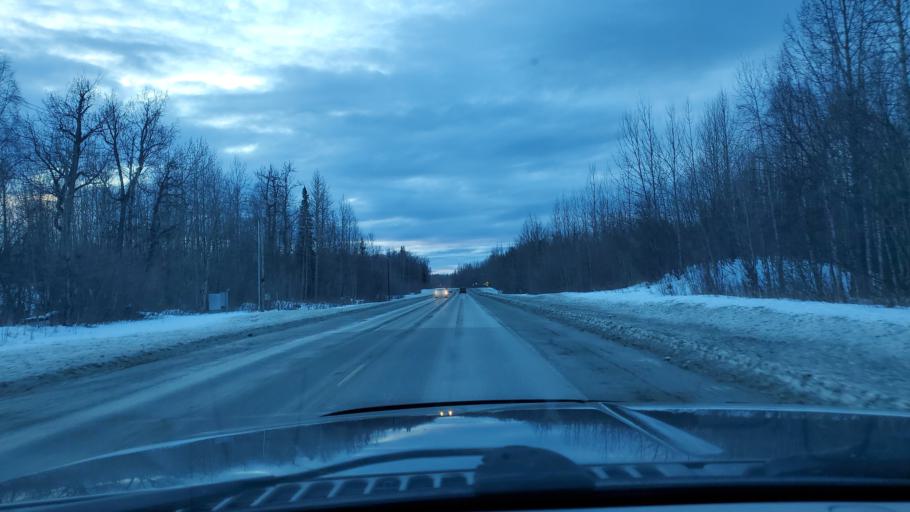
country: US
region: Alaska
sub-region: Matanuska-Susitna Borough
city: Farm Loop
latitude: 61.6717
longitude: -149.0701
